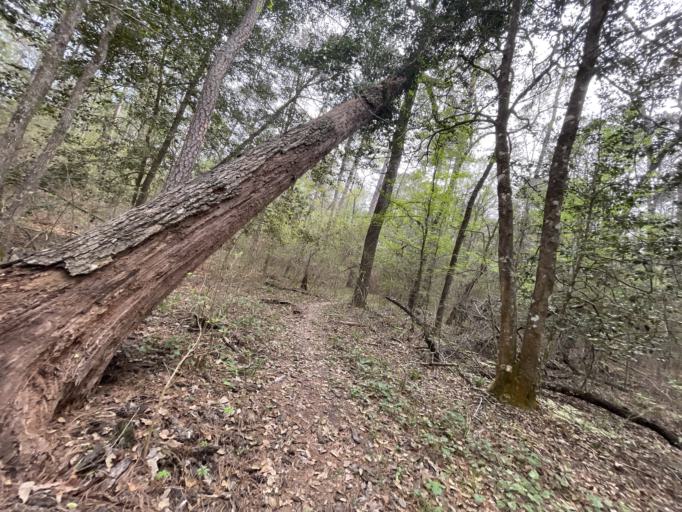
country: US
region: Texas
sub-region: Walker County
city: Huntsville
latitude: 30.6584
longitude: -95.4845
